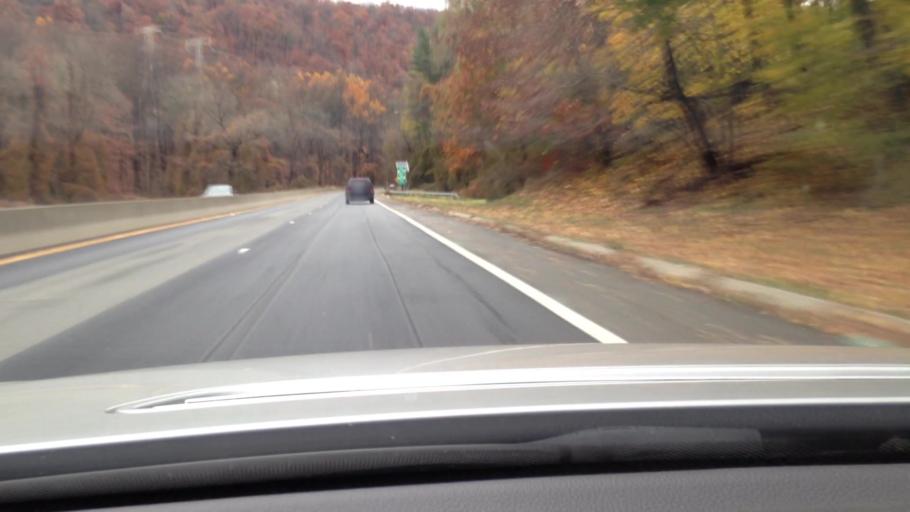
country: US
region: New York
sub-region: Westchester County
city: Hawthorne
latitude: 41.1012
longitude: -73.8109
